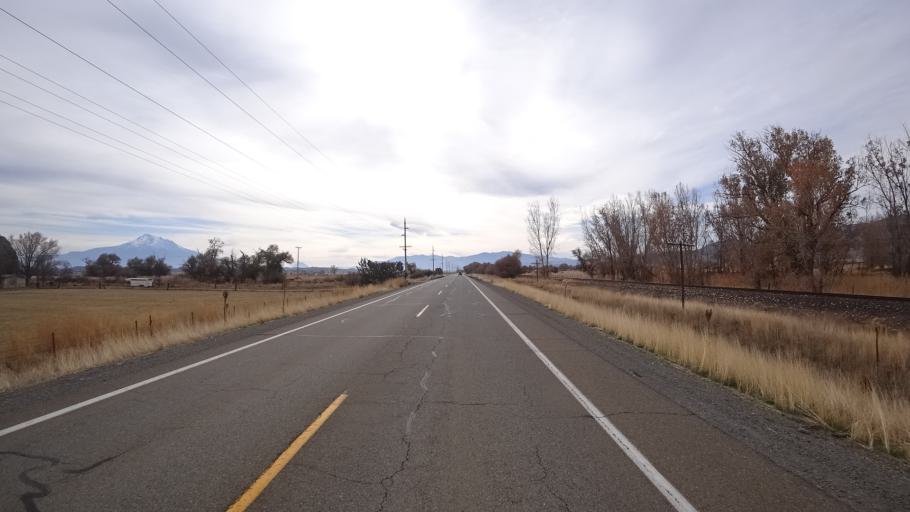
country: US
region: California
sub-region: Siskiyou County
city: Montague
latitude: 41.6558
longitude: -122.5201
